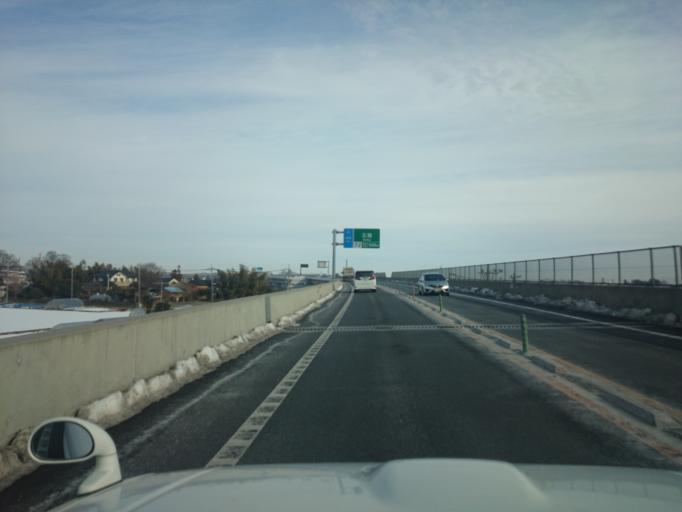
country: JP
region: Saitama
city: Satte
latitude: 36.0878
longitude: 139.7606
